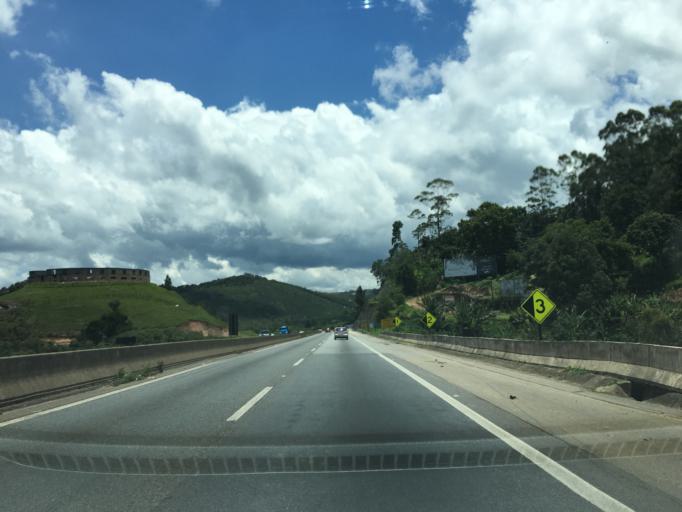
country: BR
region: Sao Paulo
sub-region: Mairipora
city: Mairipora
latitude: -23.2831
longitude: -46.5882
